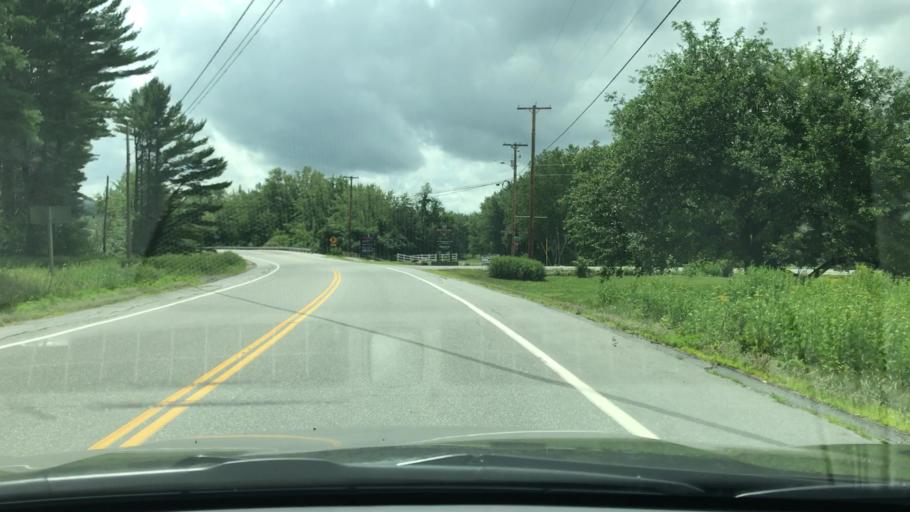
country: US
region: Maine
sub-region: Oxford County
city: Bethel
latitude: 44.4157
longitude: -70.7836
